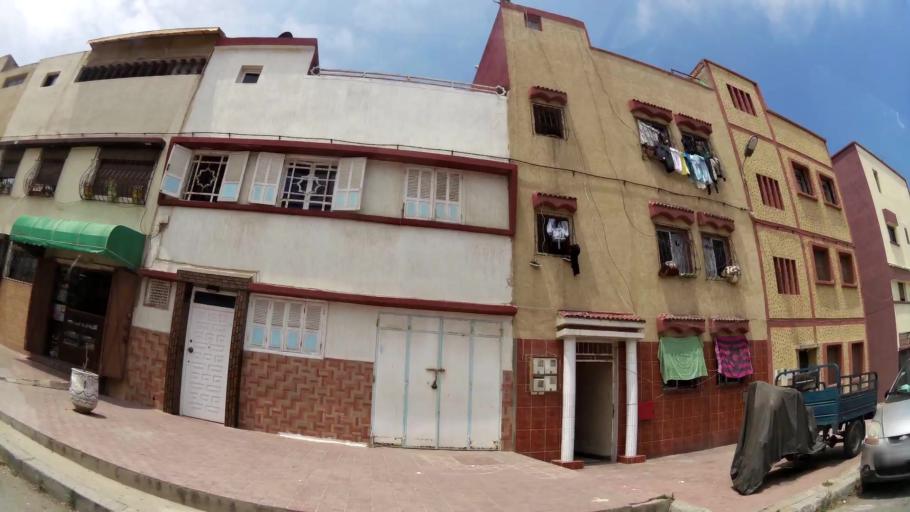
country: MA
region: Rabat-Sale-Zemmour-Zaer
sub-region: Rabat
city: Rabat
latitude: 33.9896
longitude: -6.8788
